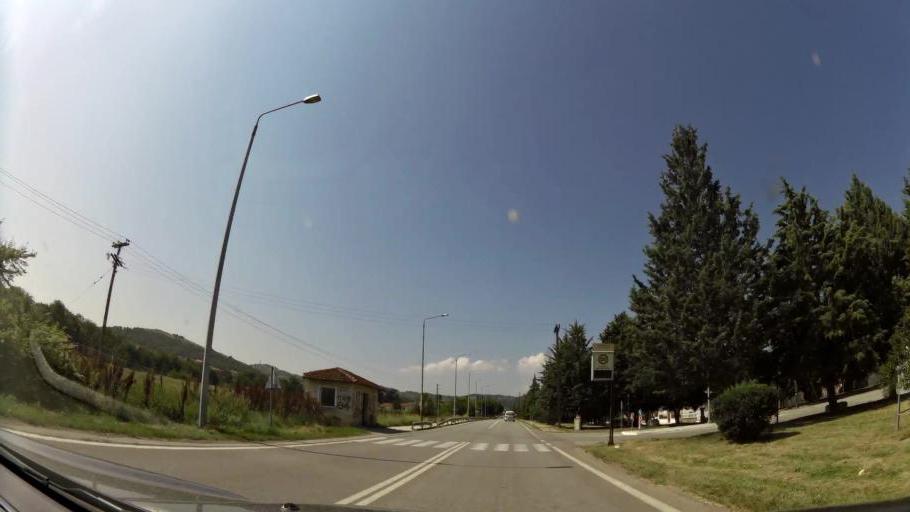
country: GR
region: West Macedonia
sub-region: Nomos Kozanis
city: Koila
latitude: 40.3358
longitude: 21.7918
